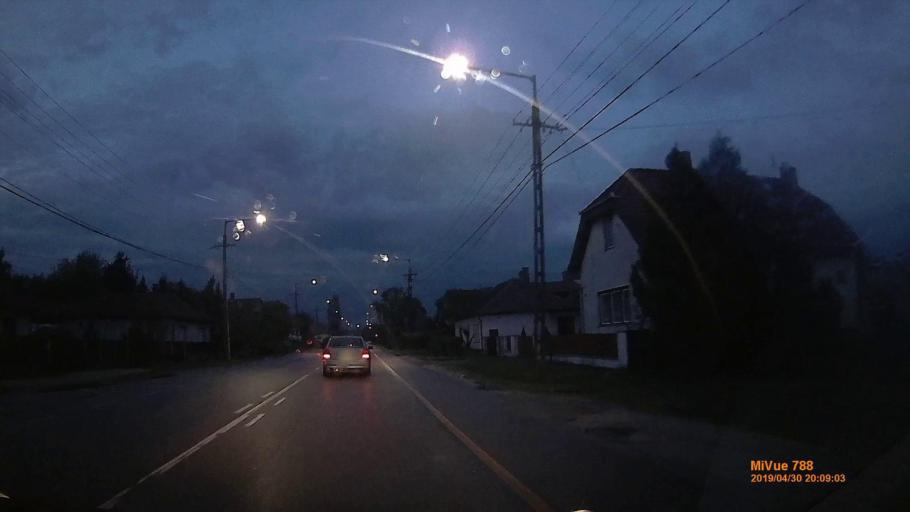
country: HU
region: Pest
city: Abony
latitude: 47.1839
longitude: 20.0519
